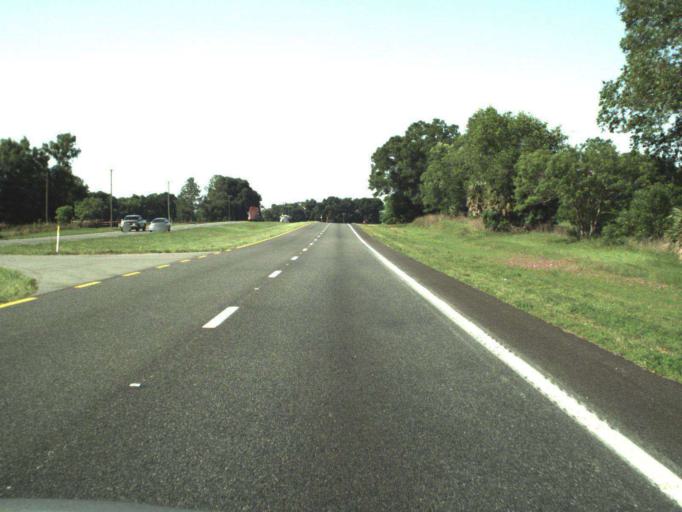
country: US
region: Florida
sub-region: Marion County
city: Citra
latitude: 29.3507
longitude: -82.1450
